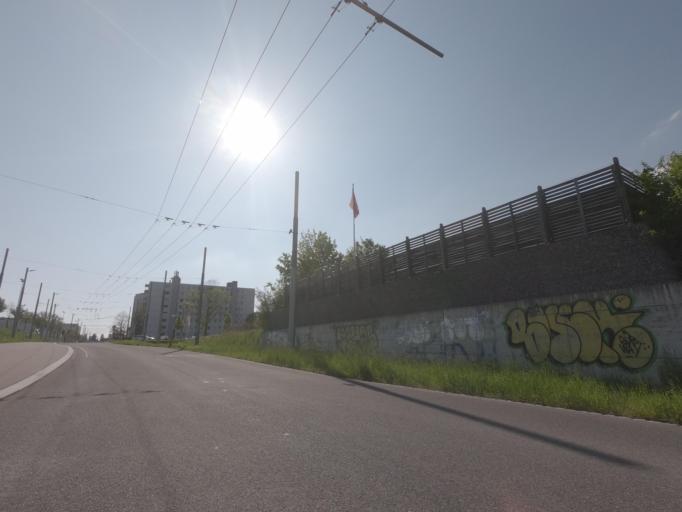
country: CH
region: Bern
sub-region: Biel/Bienne District
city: Brugg
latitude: 47.1548
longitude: 7.2781
